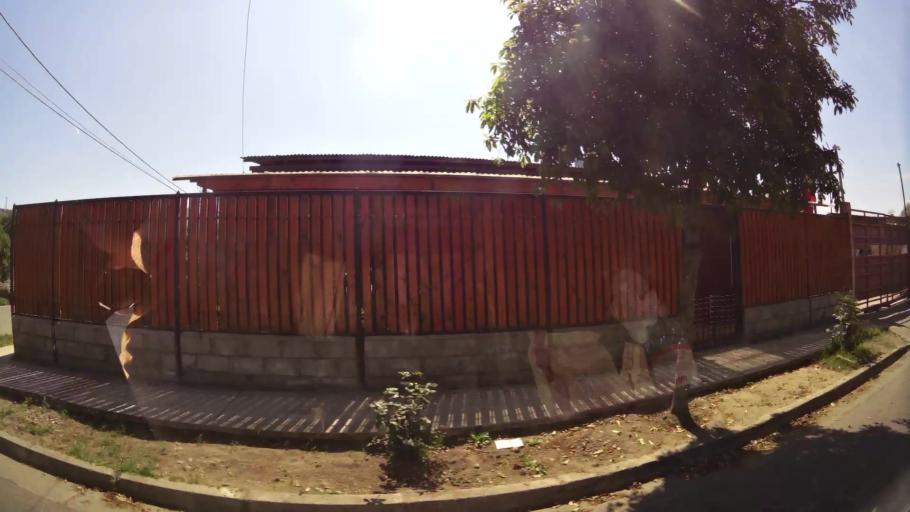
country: CL
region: Santiago Metropolitan
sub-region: Provincia de Talagante
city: Talagante
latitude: -33.6585
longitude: -70.9305
